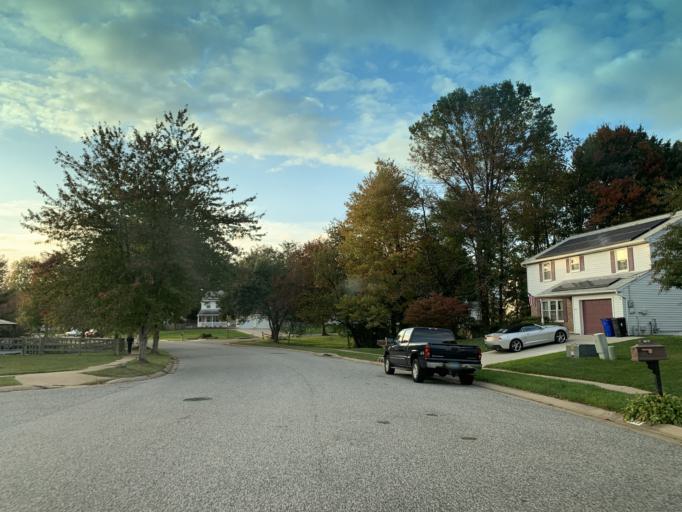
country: US
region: Maryland
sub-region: Harford County
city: South Bel Air
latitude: 39.5369
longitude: -76.3042
